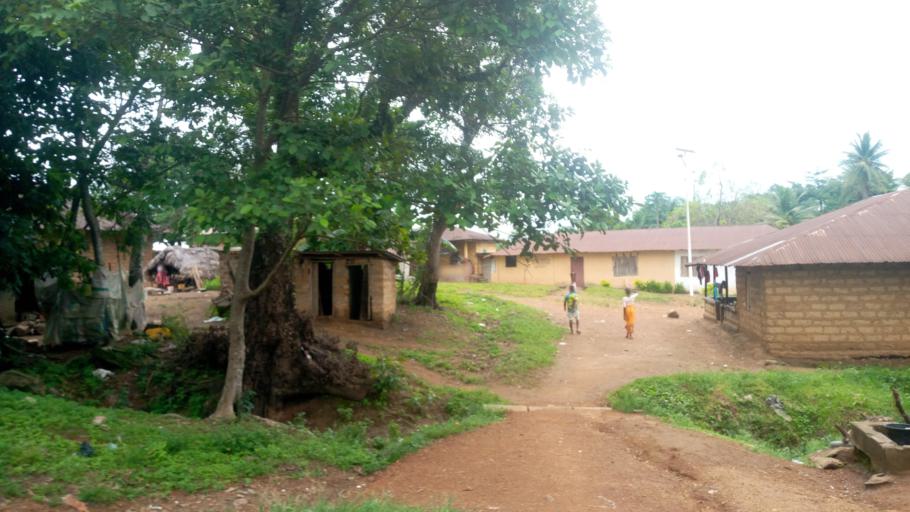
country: SL
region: Southern Province
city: Mogbwemo
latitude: 7.6048
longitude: -12.1780
